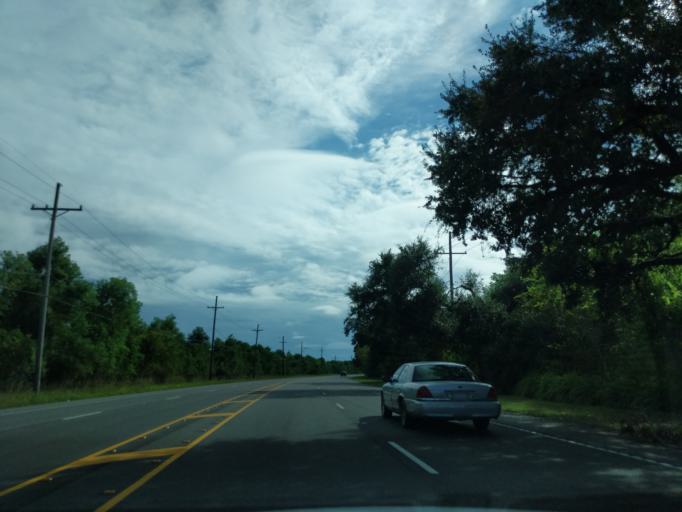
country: US
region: Louisiana
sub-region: Saint Bernard Parish
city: Meraux
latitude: 30.0659
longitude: -89.8646
